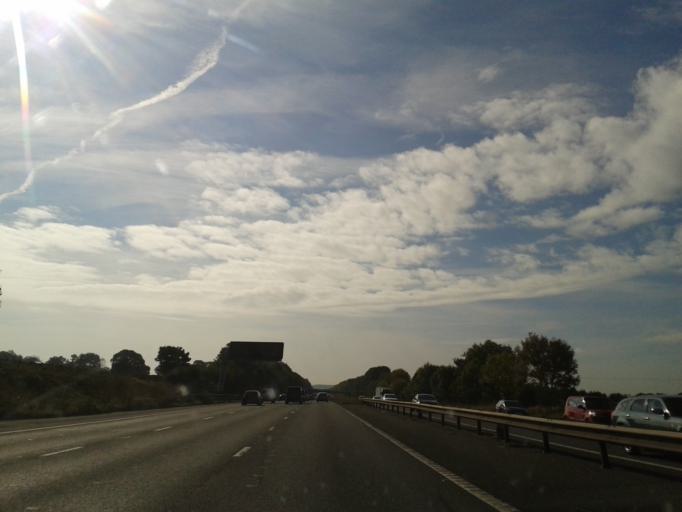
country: GB
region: England
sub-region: Staffordshire
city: Audley
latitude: 53.0594
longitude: -2.3316
